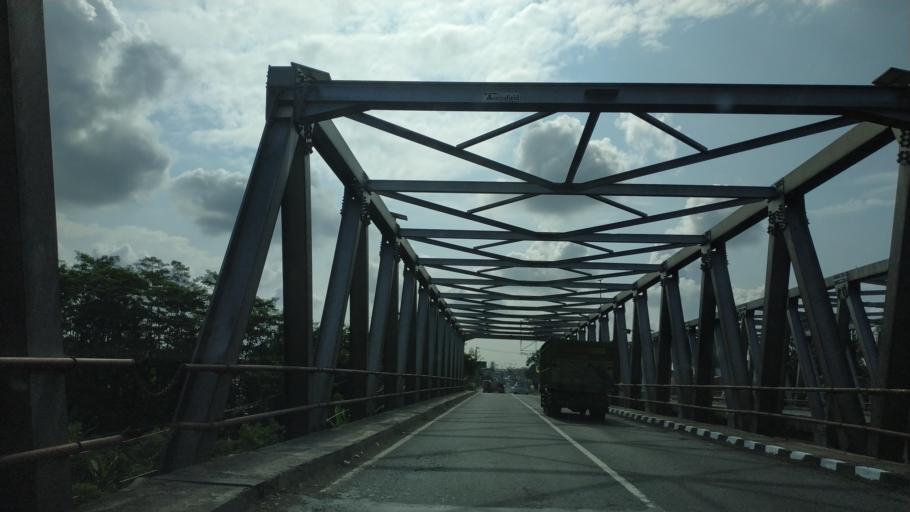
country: ID
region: Central Java
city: Comal
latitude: -6.8997
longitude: 109.5248
